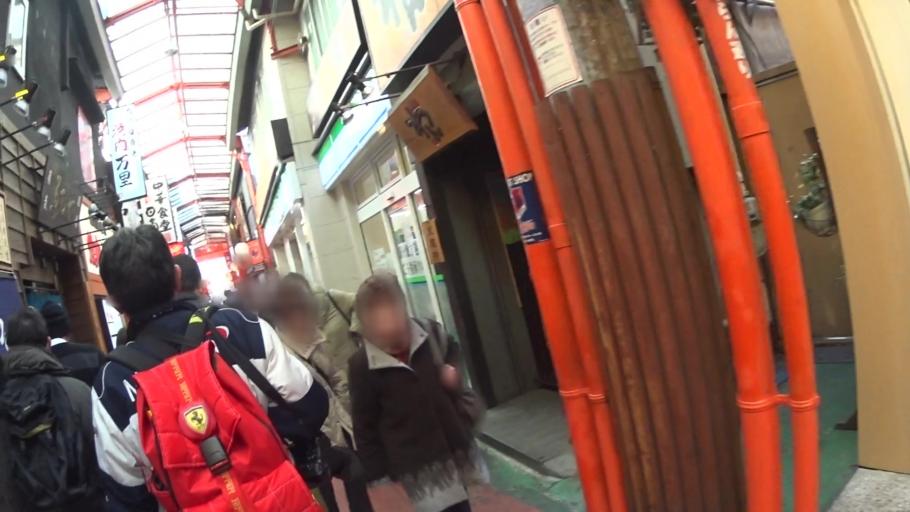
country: JP
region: Saitama
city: Yono
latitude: 35.9073
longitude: 139.6275
